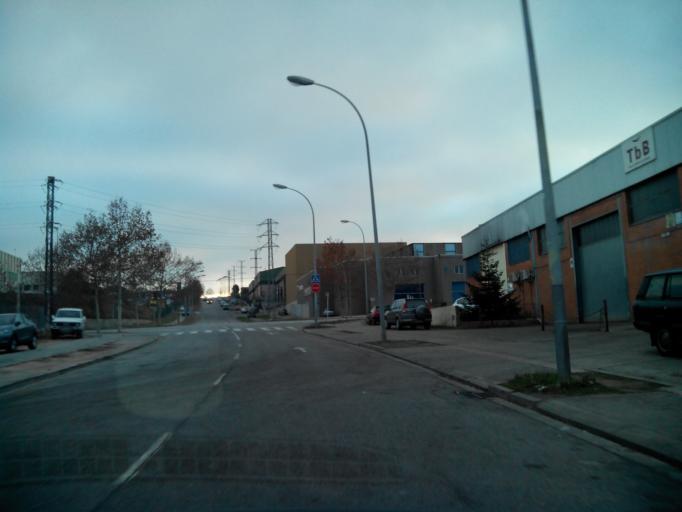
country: ES
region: Catalonia
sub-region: Provincia de Barcelona
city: Manresa
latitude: 41.7120
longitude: 1.8467
